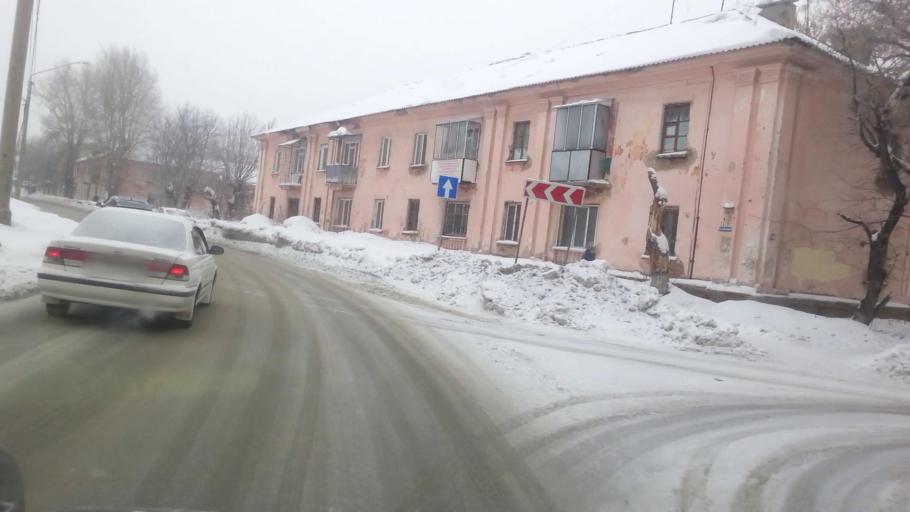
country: RU
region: Altai Krai
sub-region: Gorod Barnaulskiy
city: Barnaul
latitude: 53.3793
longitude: 83.7293
